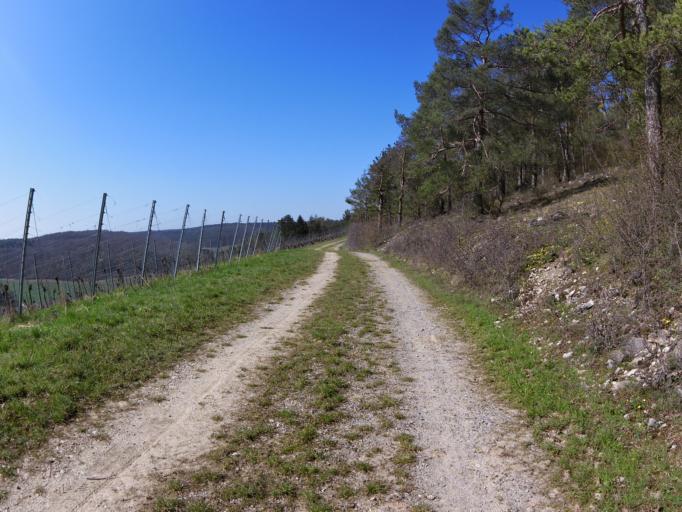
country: DE
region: Bavaria
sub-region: Regierungsbezirk Unterfranken
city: Erlabrunn
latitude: 49.8465
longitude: 9.8142
